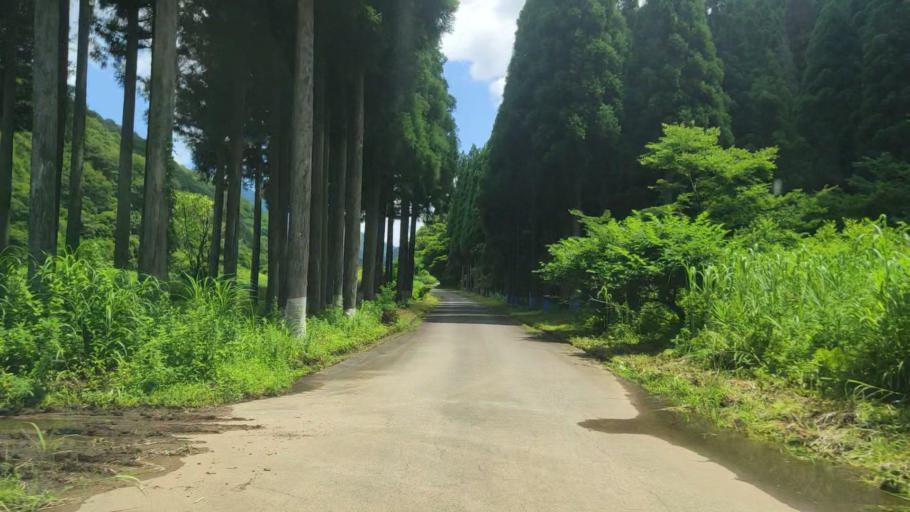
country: JP
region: Fukui
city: Ono
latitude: 35.8086
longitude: 136.4663
